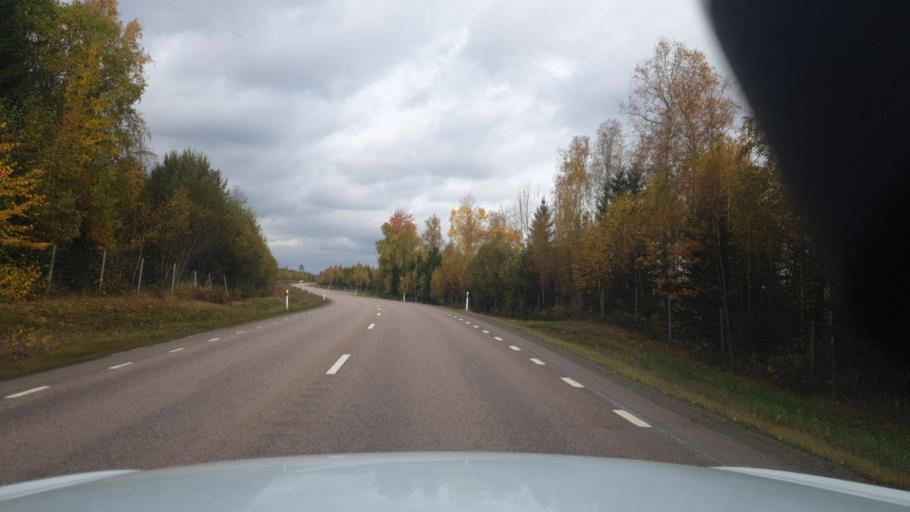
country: SE
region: Vaermland
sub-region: Sunne Kommun
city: Sunne
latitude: 59.7433
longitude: 13.1278
